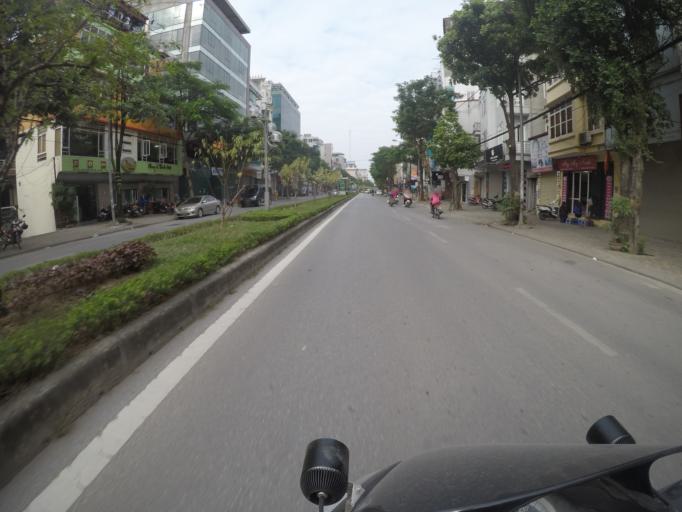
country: VN
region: Ha Noi
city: Tay Ho
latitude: 21.0641
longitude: 105.8097
